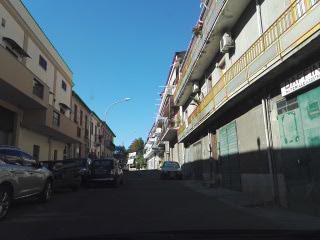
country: IT
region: Calabria
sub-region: Provincia di Vibo-Valentia
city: Sorianello
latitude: 38.5952
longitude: 16.2314
